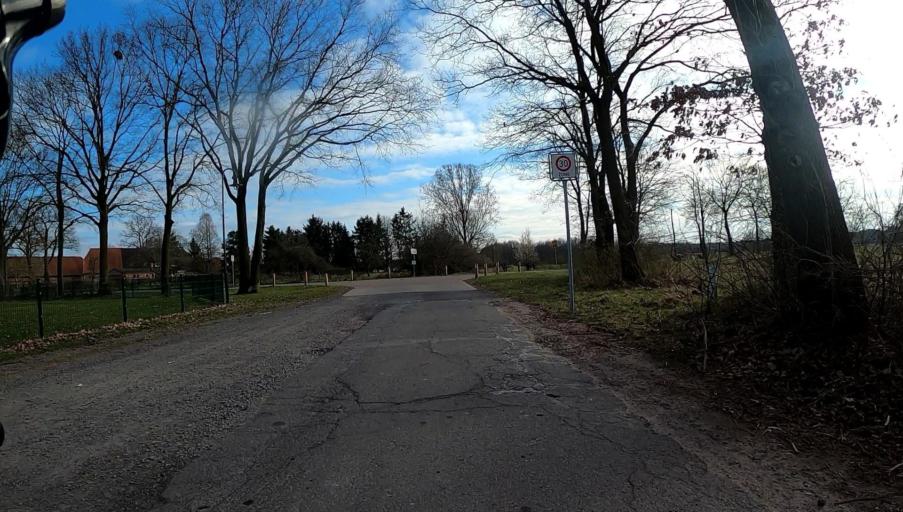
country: DE
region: Lower Saxony
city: Lindwedel
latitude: 52.6067
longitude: 9.6829
